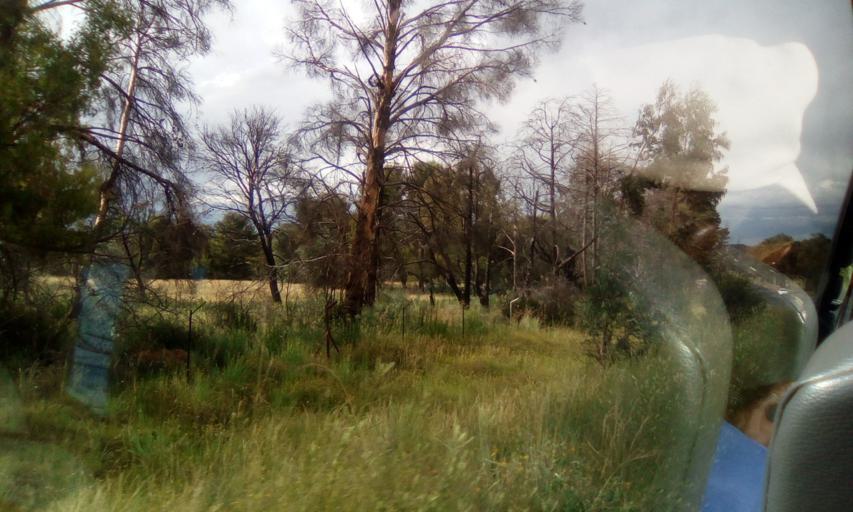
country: ZA
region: Orange Free State
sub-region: Thabo Mofutsanyana District Municipality
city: Ladybrand
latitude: -29.2102
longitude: 27.4666
